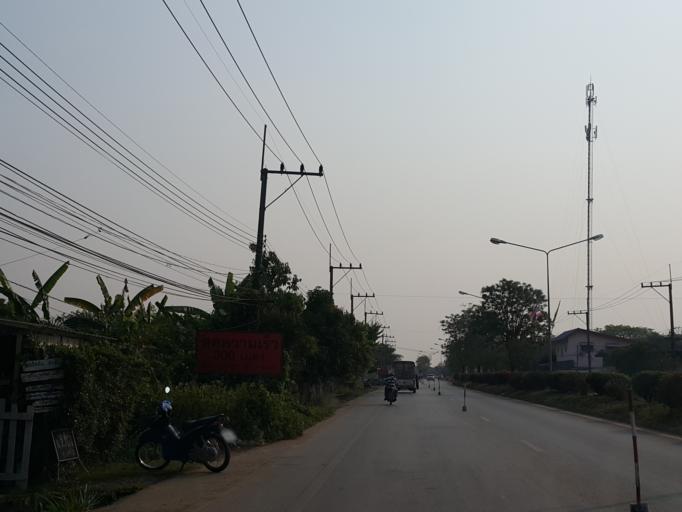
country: TH
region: Lampang
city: Lampang
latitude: 18.3378
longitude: 99.5330
